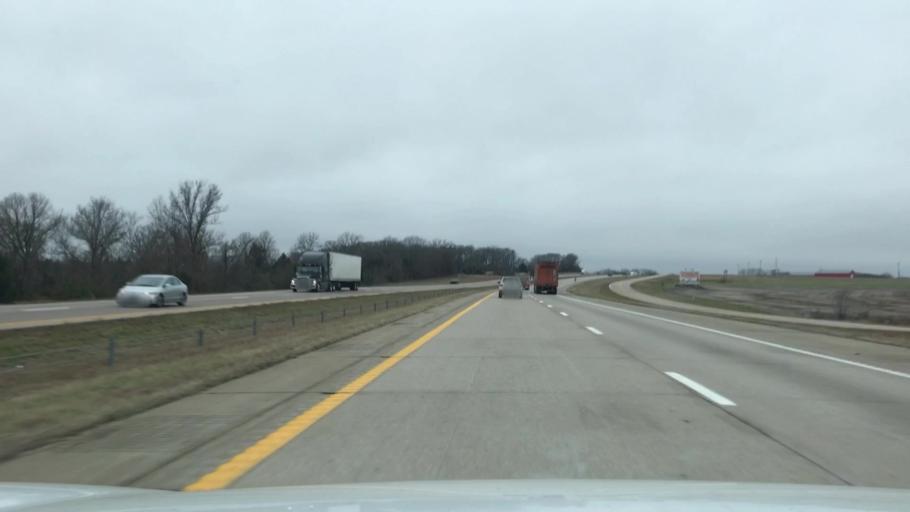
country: US
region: Missouri
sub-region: Crawford County
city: Bourbon
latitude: 38.1418
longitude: -91.2708
